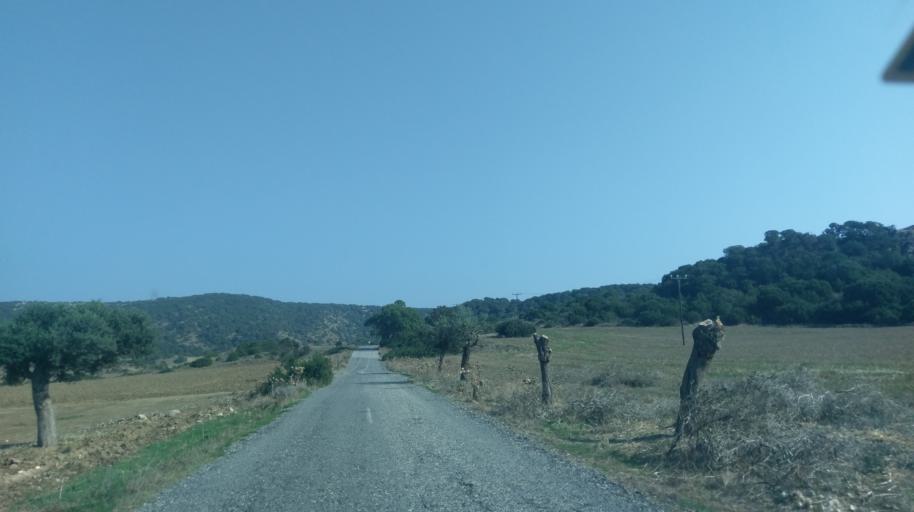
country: CY
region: Ammochostos
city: Rizokarpaso
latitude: 35.6477
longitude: 34.5443
